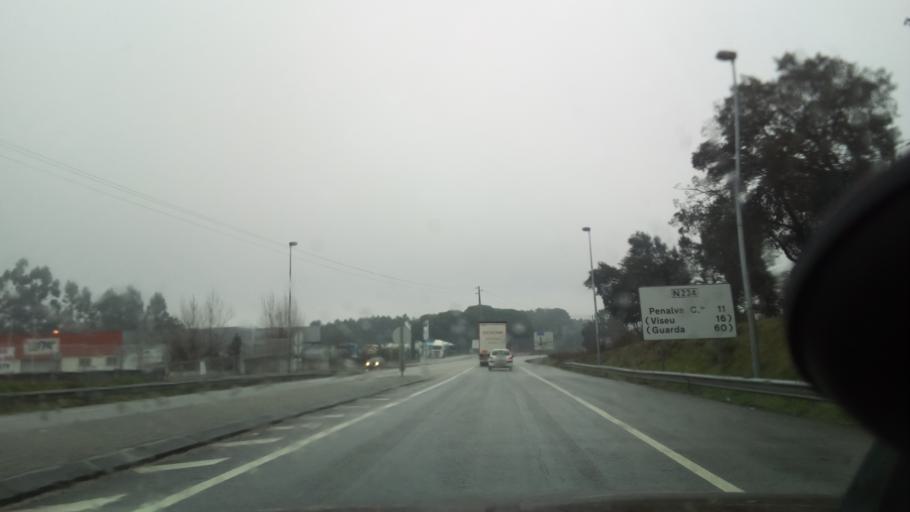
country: PT
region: Viseu
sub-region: Mangualde
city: Mangualde
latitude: 40.6100
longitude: -7.7778
